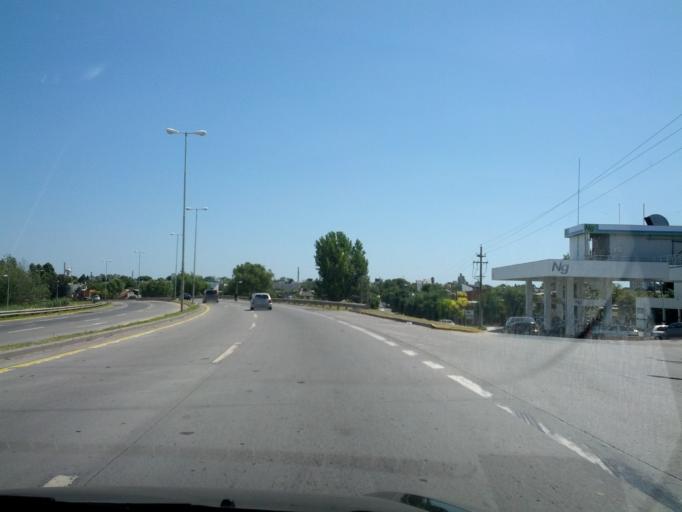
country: AR
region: Buenos Aires
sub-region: Partido de Campana
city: Campana
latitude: -34.1719
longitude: -58.9713
